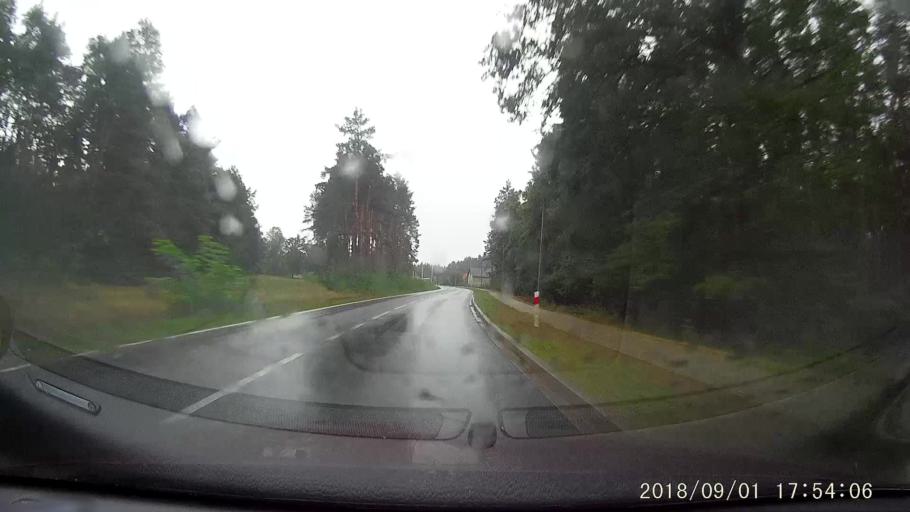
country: PL
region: Lubusz
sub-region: Powiat zaganski
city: Ilowa
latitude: 51.4718
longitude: 15.1994
